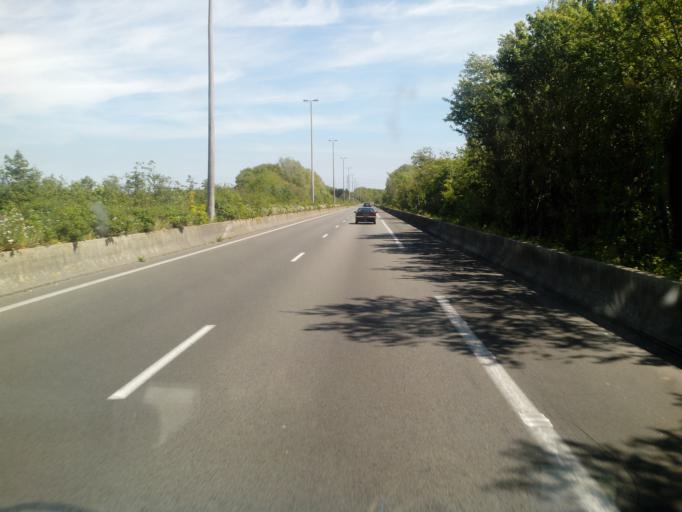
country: FR
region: Nord-Pas-de-Calais
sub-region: Departement du Pas-de-Calais
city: Saint-Martin-Boulogne
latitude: 50.7361
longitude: 1.6362
